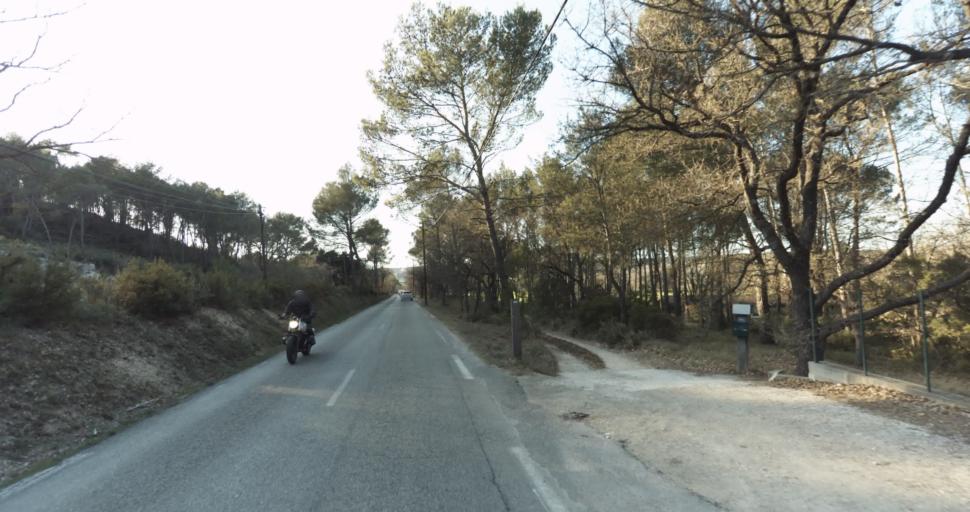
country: FR
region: Provence-Alpes-Cote d'Azur
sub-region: Departement des Bouches-du-Rhone
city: Ventabren
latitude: 43.5076
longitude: 5.3321
